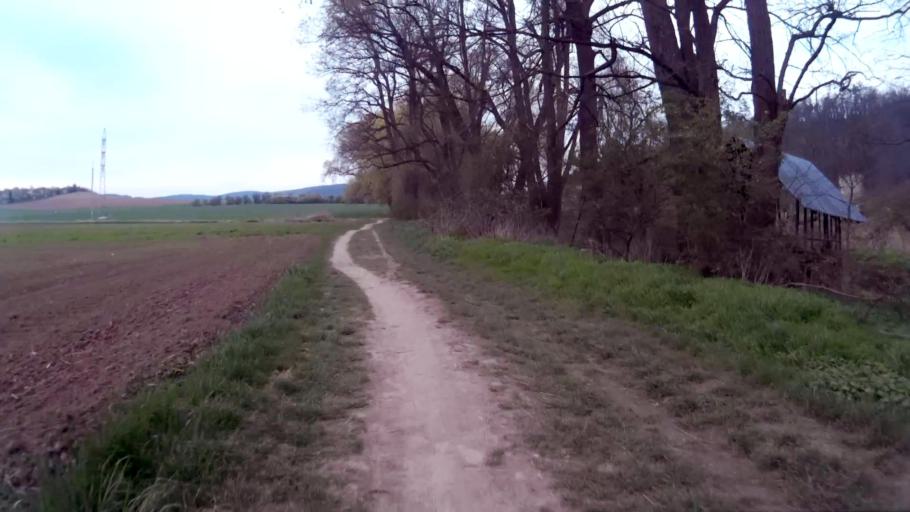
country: CZ
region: South Moravian
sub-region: Mesto Brno
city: Mokra Hora
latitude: 49.2264
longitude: 16.5614
